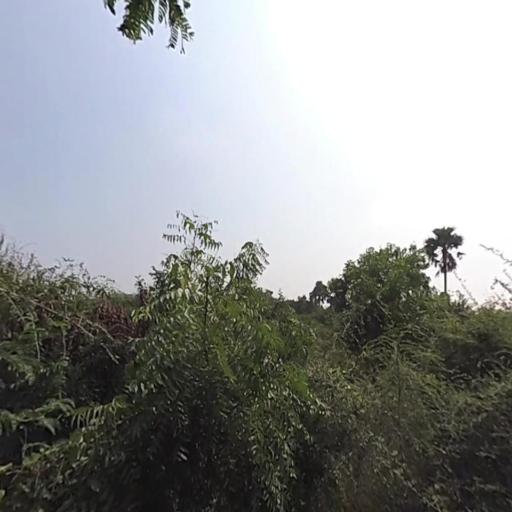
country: IN
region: Telangana
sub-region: Nalgonda
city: Nalgonda
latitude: 17.2055
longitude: 79.1531
